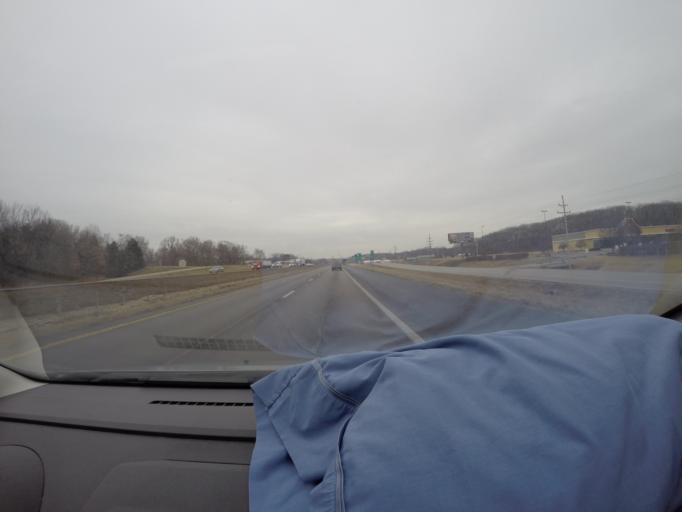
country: US
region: Missouri
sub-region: Warren County
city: Warrenton
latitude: 38.8198
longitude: -91.1624
